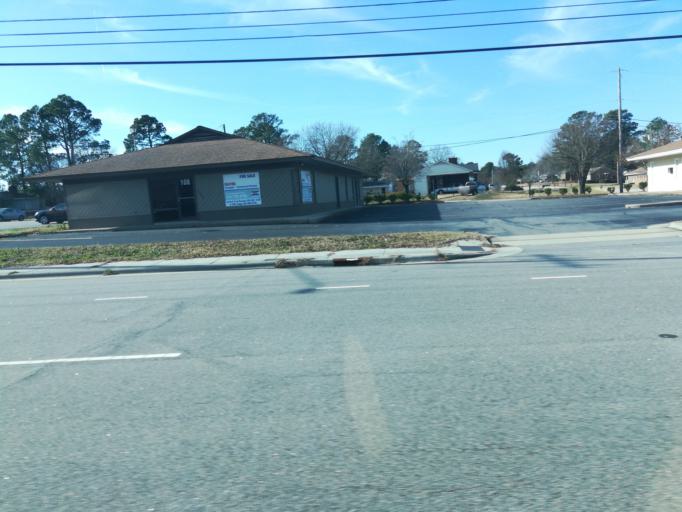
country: US
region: North Carolina
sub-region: Nash County
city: Rocky Mount
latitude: 35.9647
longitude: -77.8496
